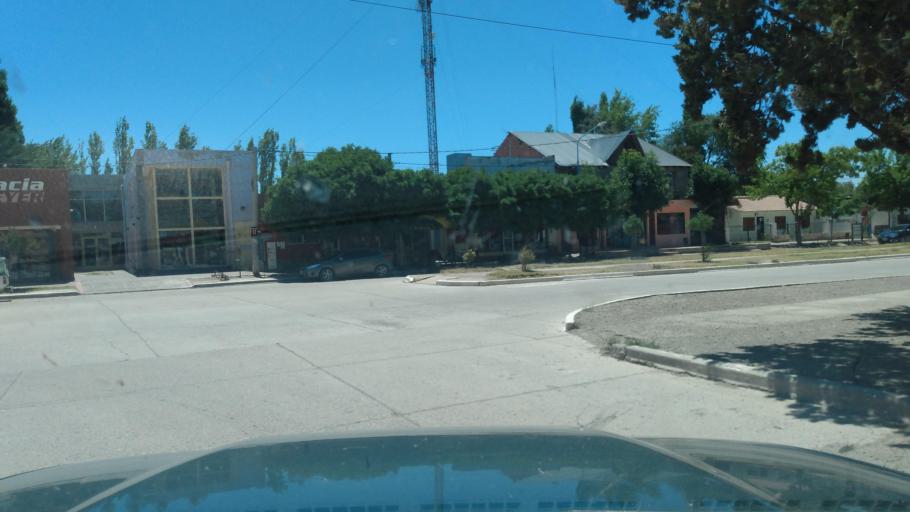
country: AR
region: Neuquen
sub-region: Departamento de Picun Leufu
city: Picun Leufu
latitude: -39.5184
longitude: -69.2903
